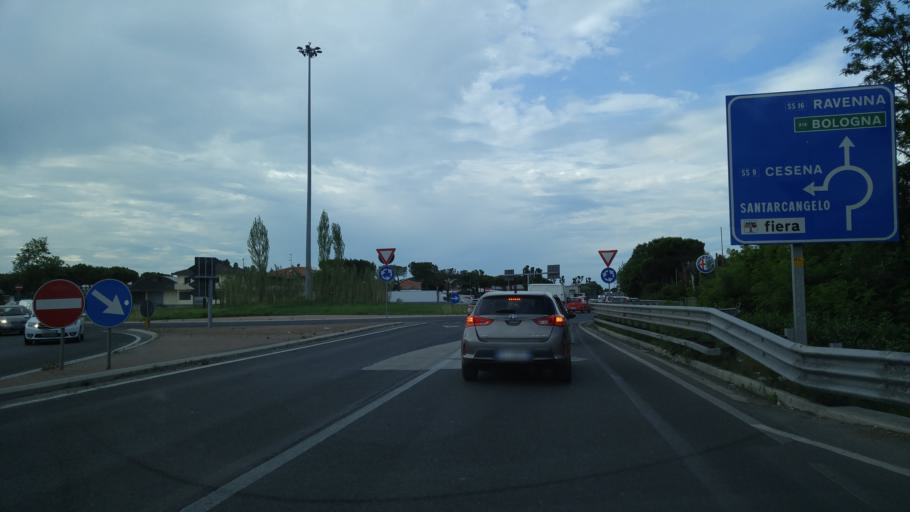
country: IT
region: Emilia-Romagna
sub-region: Provincia di Rimini
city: Rimini
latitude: 44.0633
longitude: 12.5418
